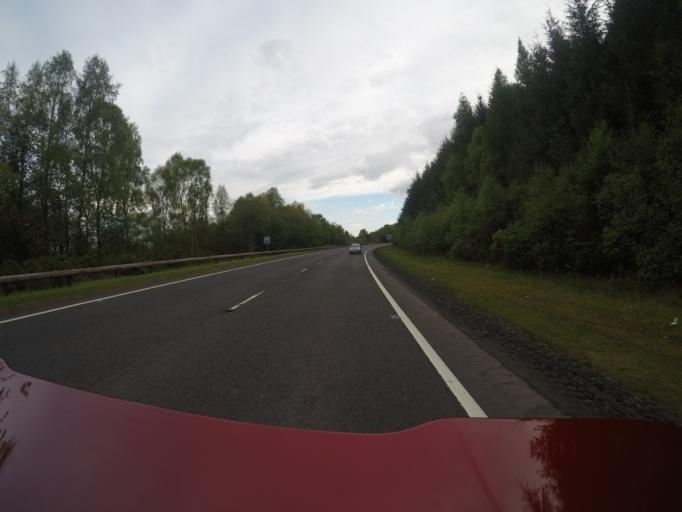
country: GB
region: Scotland
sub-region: West Dunbartonshire
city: Balloch
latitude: 56.1071
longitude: -4.6392
